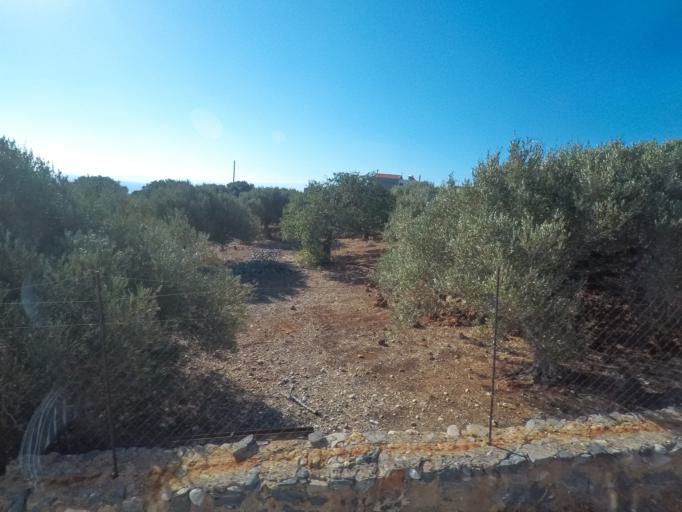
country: GR
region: Crete
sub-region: Nomos Lasithiou
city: Skhisma
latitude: 35.2449
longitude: 25.7258
